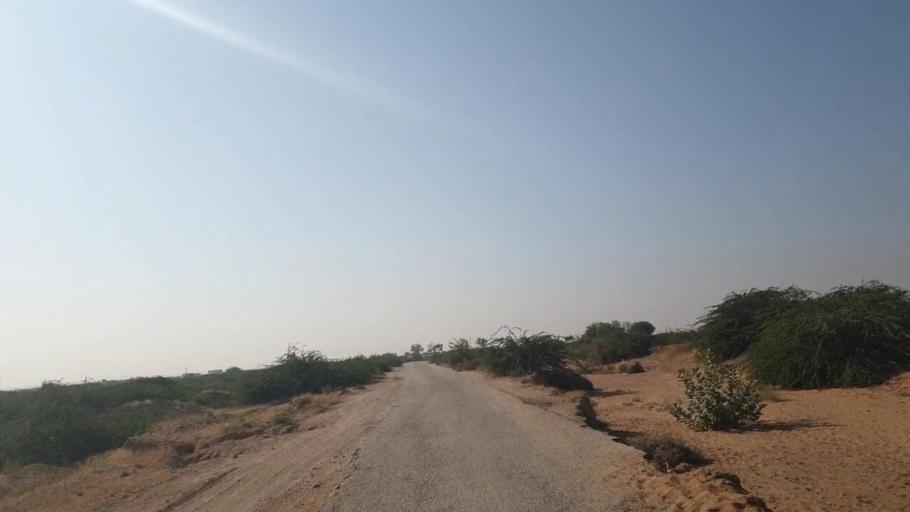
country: PK
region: Sindh
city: Thatta
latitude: 25.1414
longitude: 67.7724
